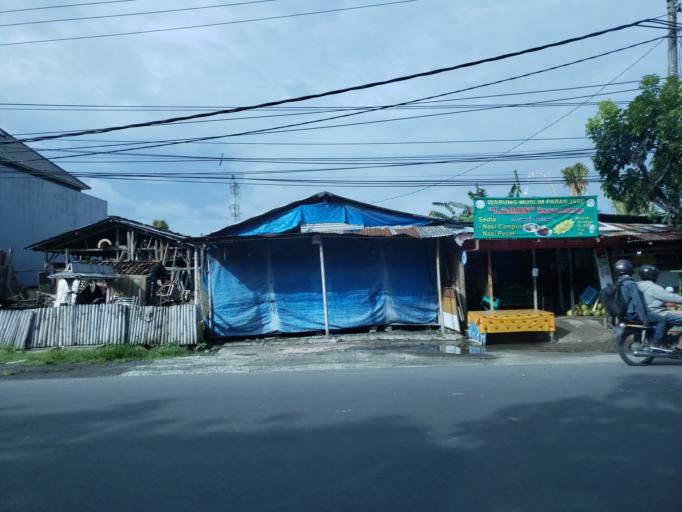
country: ID
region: Bali
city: Denpasar
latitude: -8.6763
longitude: 115.1855
